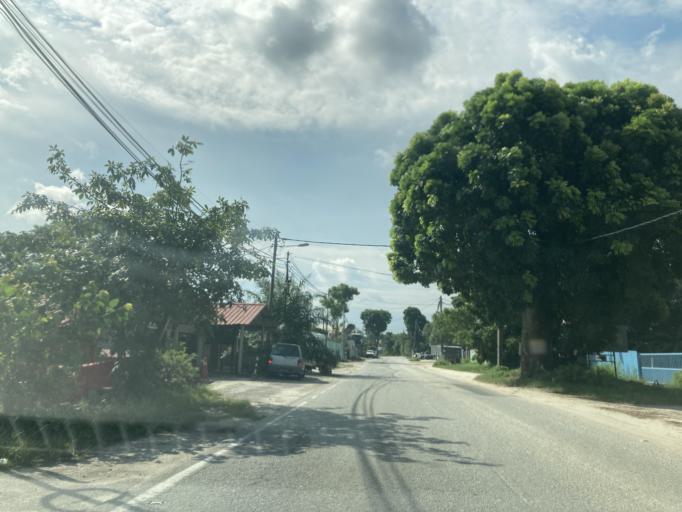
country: MY
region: Selangor
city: Kampung Baru Subang
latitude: 3.1438
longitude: 101.5450
